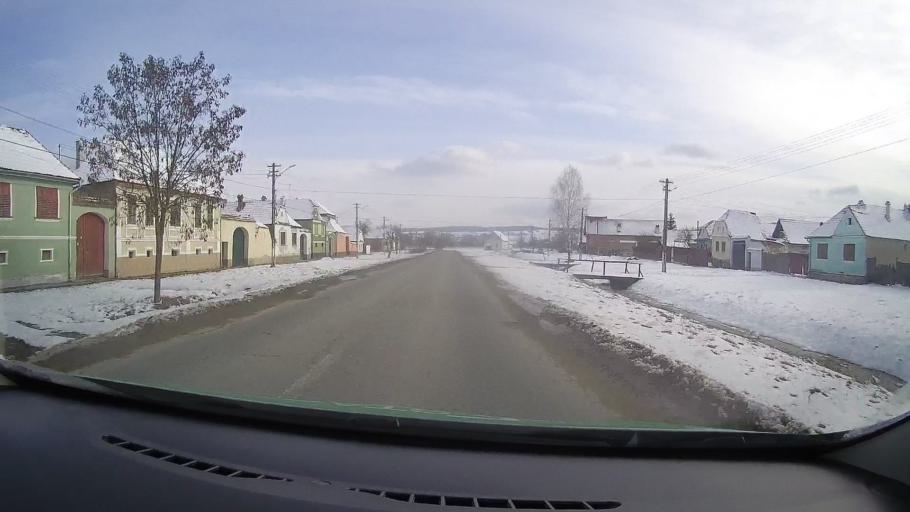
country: RO
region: Sibiu
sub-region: Comuna Merghindeal
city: Merghindeal
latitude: 45.9821
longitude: 24.6959
